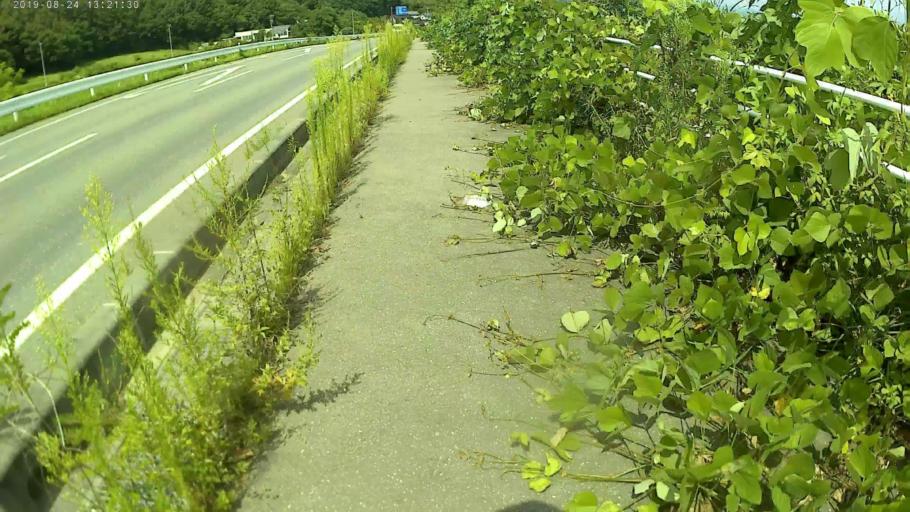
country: JP
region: Nagano
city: Komoro
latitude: 36.2707
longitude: 138.3829
